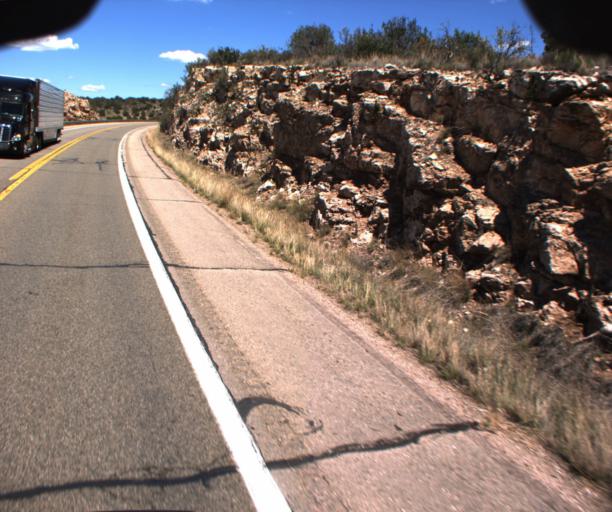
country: US
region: Arizona
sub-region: Yavapai County
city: Paulden
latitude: 34.9232
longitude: -112.4520
